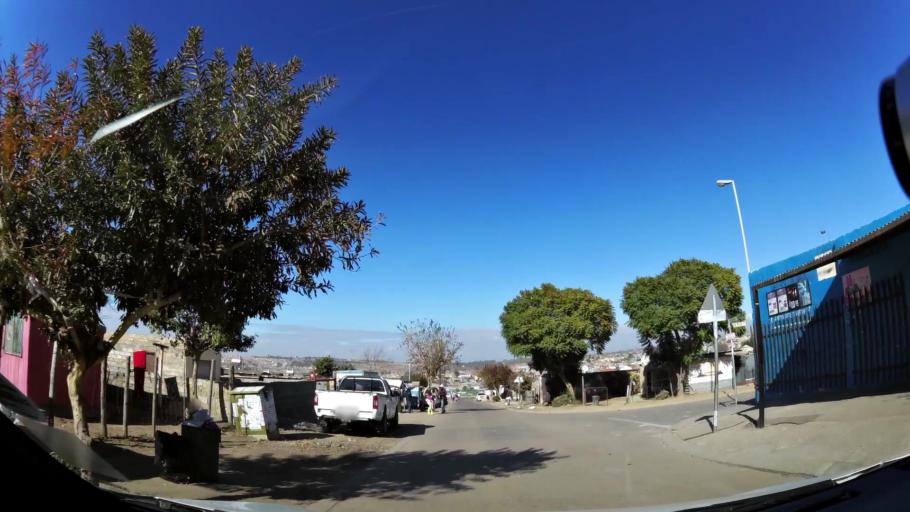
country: ZA
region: Gauteng
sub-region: City of Johannesburg Metropolitan Municipality
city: Diepsloot
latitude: -25.9095
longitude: 28.0930
